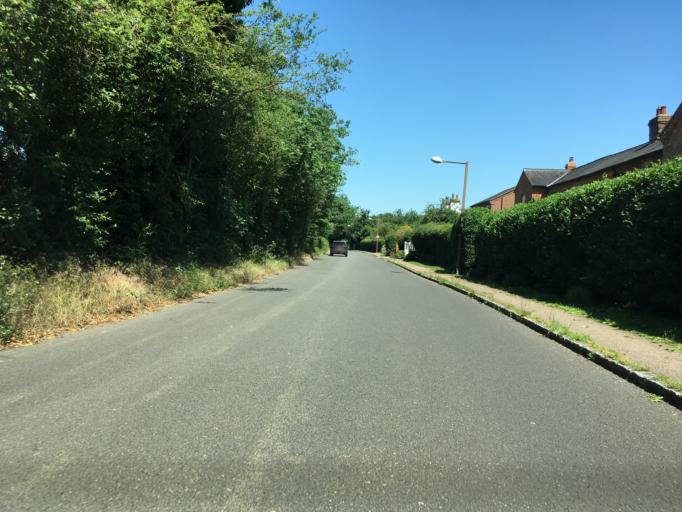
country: GB
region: England
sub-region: Milton Keynes
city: Simpson
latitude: 52.0332
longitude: -0.7239
